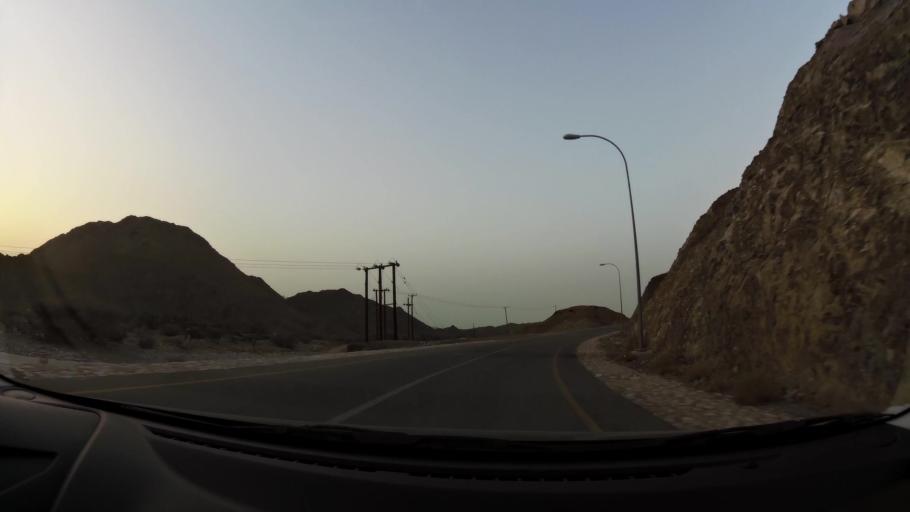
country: OM
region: Muhafazat Masqat
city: Bawshar
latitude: 23.4841
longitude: 58.3296
